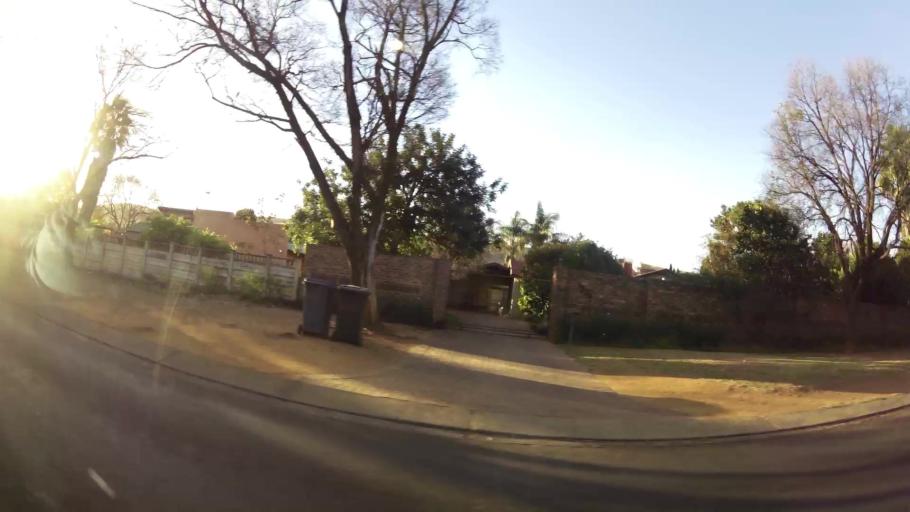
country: ZA
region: Gauteng
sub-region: City of Tshwane Metropolitan Municipality
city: Pretoria
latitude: -25.7017
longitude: 28.2477
